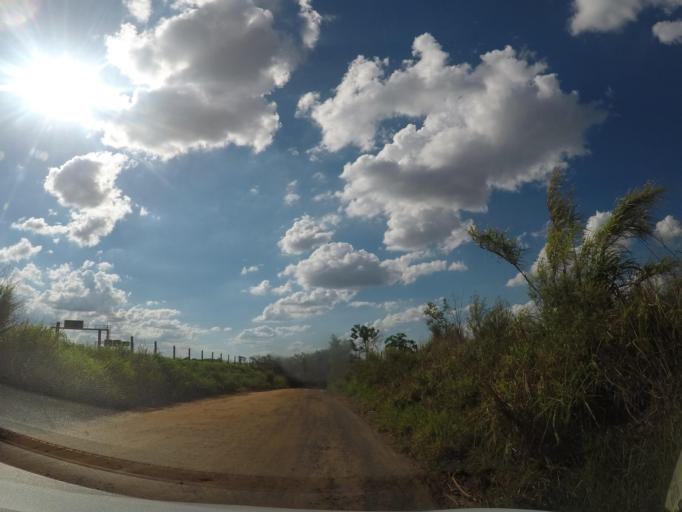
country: BR
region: Sao Paulo
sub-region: Sumare
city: Sumare
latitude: -22.8497
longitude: -47.3270
